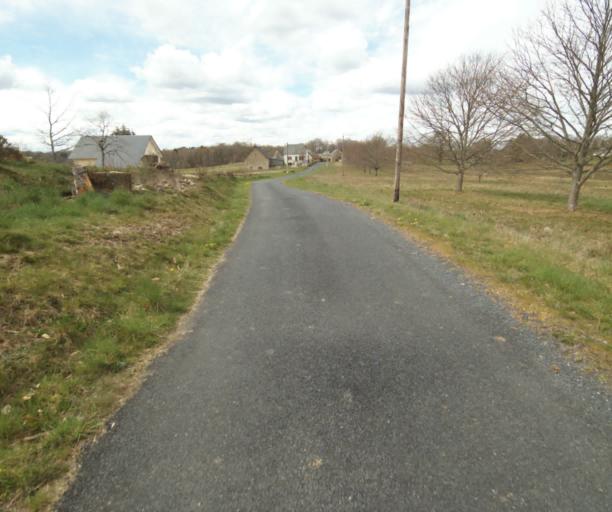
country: FR
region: Limousin
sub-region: Departement de la Correze
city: Argentat
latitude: 45.2181
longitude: 1.9233
